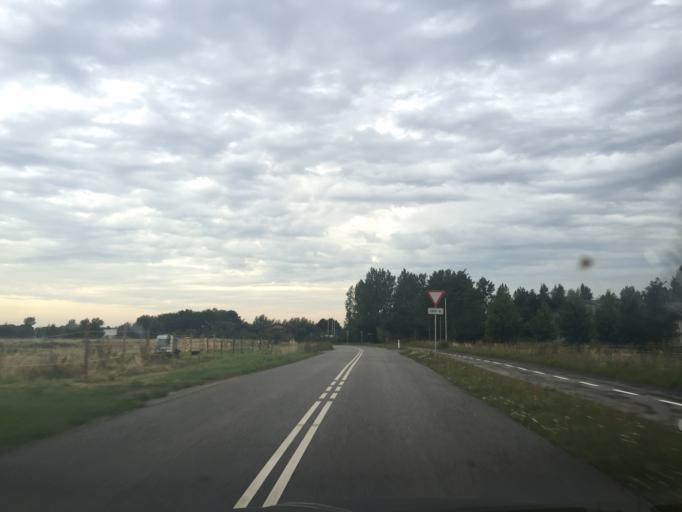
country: DK
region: Zealand
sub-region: Roskilde Kommune
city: Jyllinge
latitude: 55.7544
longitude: 12.1325
